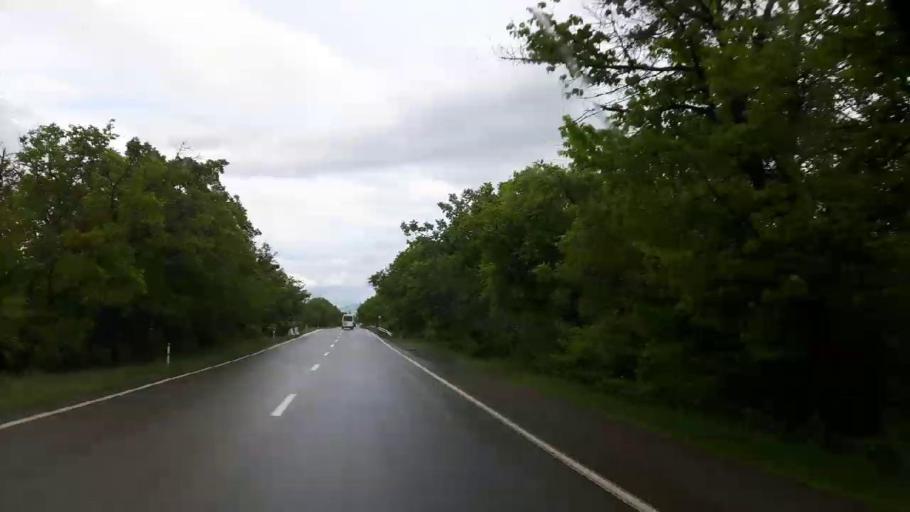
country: GE
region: Shida Kartli
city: Kaspi
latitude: 41.9547
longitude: 44.4918
